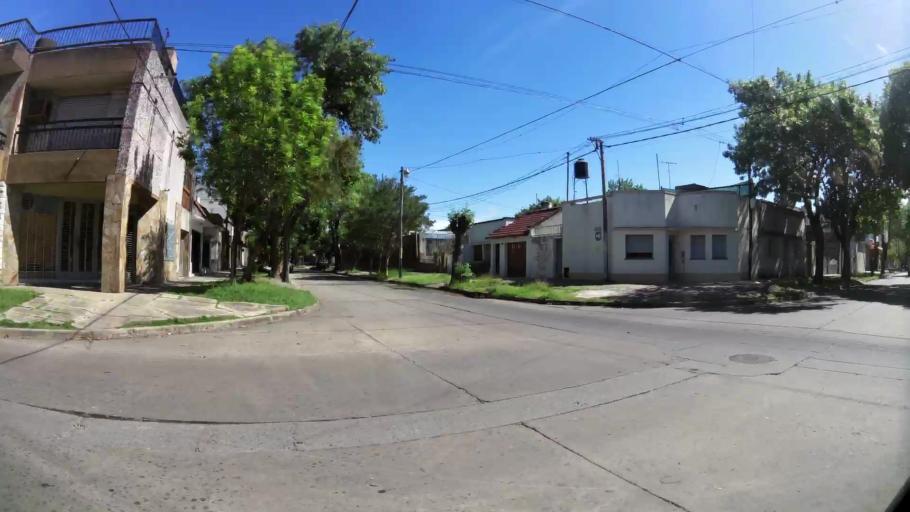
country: AR
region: Santa Fe
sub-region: Departamento de Rosario
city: Rosario
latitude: -32.9387
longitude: -60.6986
